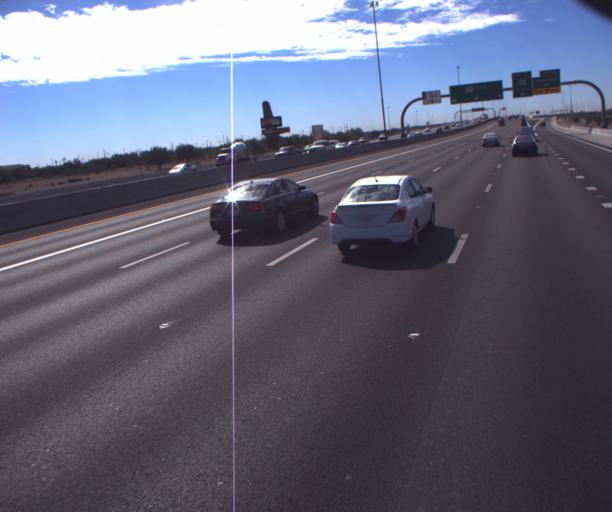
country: US
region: Arizona
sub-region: Maricopa County
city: Tempe
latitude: 33.4573
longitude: -111.8898
